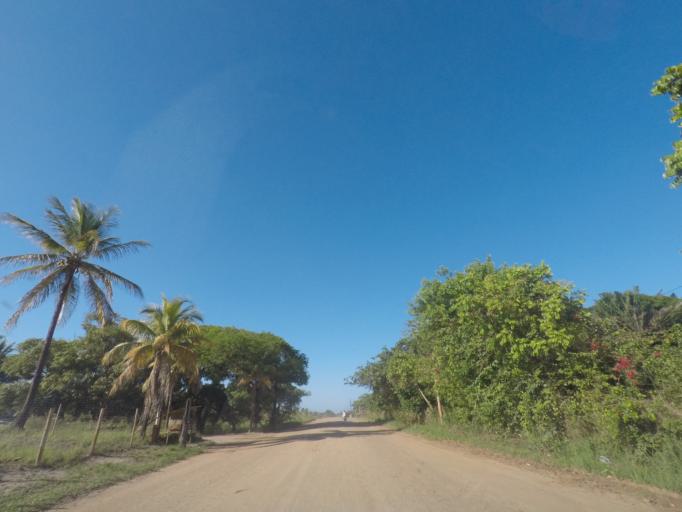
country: BR
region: Bahia
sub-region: Marau
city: Marau
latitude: -14.0386
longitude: -38.9553
